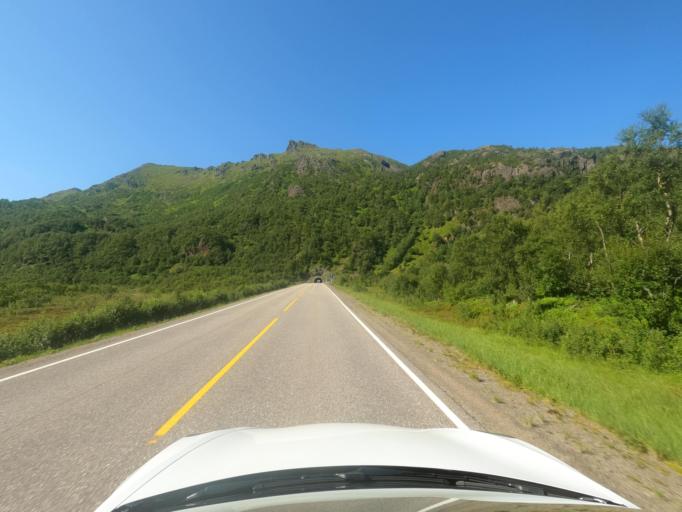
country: NO
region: Nordland
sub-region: Sortland
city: Sortland
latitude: 68.4608
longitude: 15.2551
